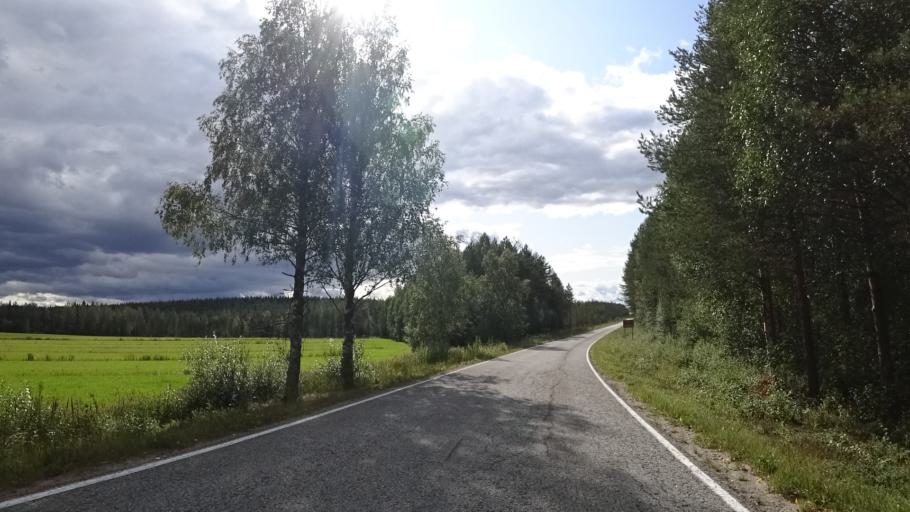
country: FI
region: North Karelia
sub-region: Joensuu
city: Ilomantsi
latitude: 62.4451
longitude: 31.1107
